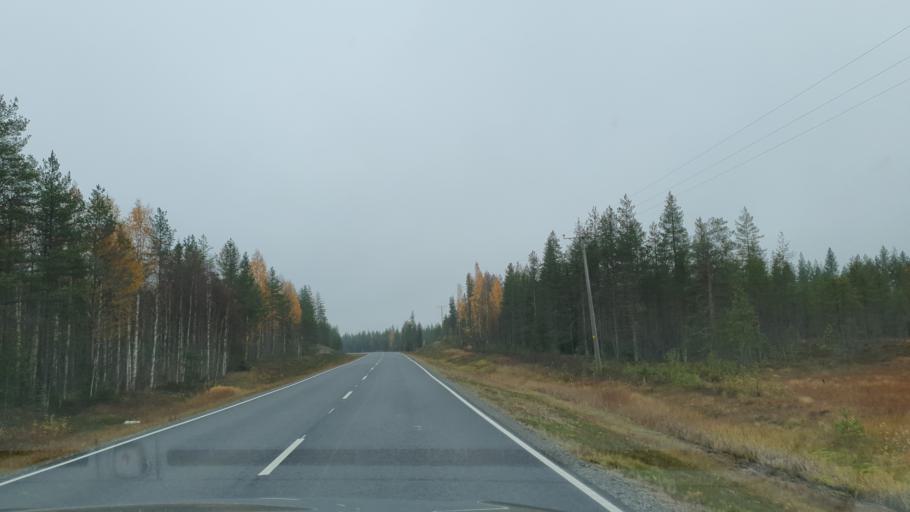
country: FI
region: Lapland
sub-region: Rovaniemi
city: Ranua
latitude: 66.1366
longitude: 26.2752
